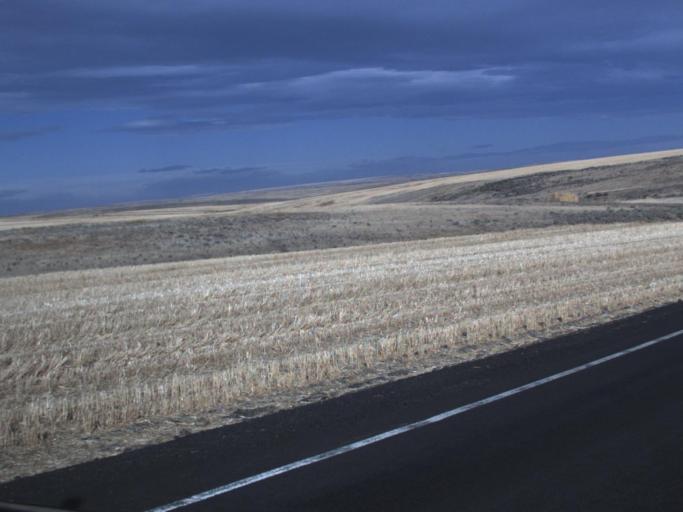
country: US
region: Washington
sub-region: Adams County
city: Ritzville
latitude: 47.2881
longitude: -118.6902
